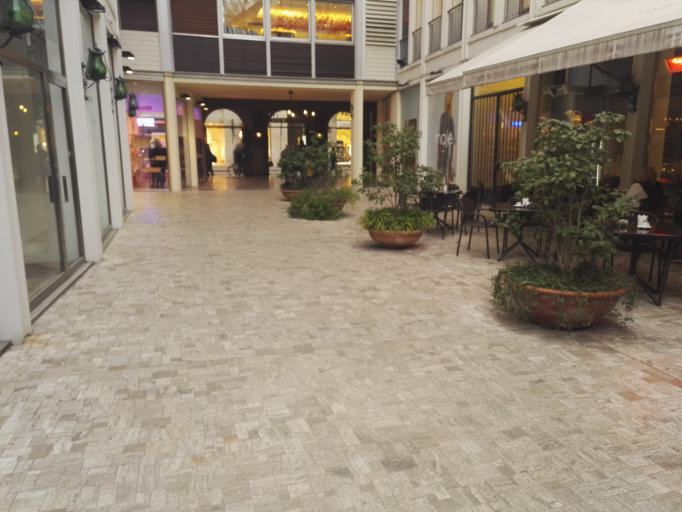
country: IT
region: Lombardy
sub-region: Citta metropolitana di Milano
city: Milano
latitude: 45.4690
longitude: 9.1925
